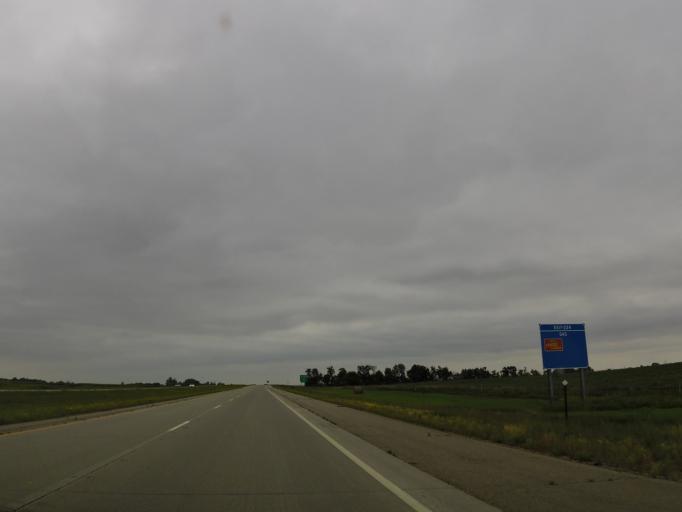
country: US
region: South Dakota
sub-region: Roberts County
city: Sisseton
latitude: 45.5366
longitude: -96.9892
